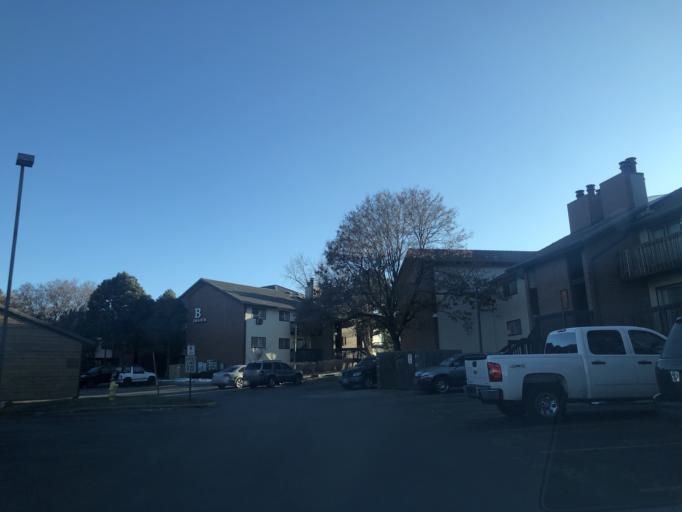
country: US
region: Colorado
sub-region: Adams County
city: Aurora
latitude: 39.7195
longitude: -104.8187
